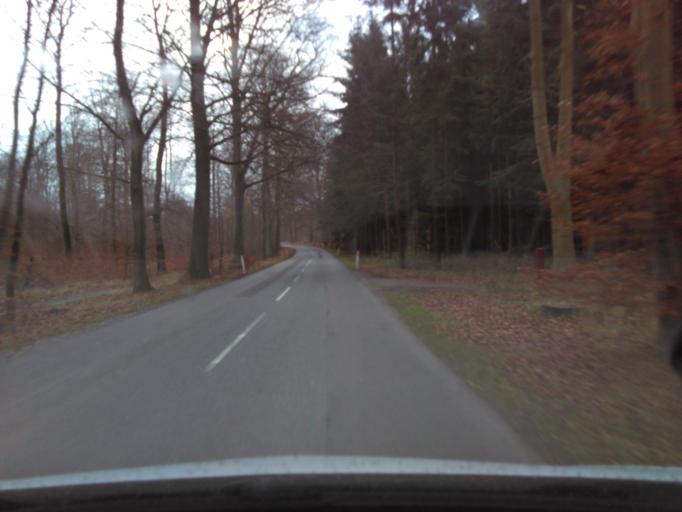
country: DK
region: Capital Region
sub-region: Fureso Kommune
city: Vaerlose
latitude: 55.7692
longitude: 12.3837
